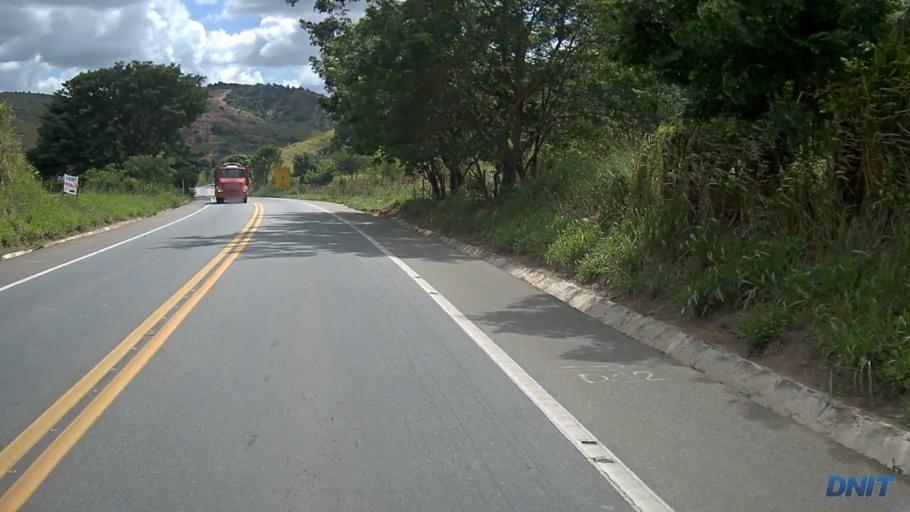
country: BR
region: Minas Gerais
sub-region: Governador Valadares
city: Governador Valadares
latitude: -18.9515
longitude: -42.0714
